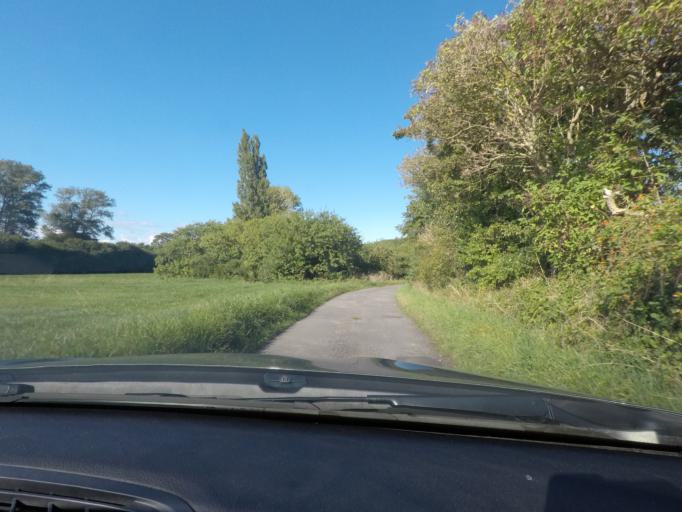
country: DK
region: Zealand
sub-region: Guldborgsund Kommune
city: Sakskobing
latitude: 54.9739
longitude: 11.5328
